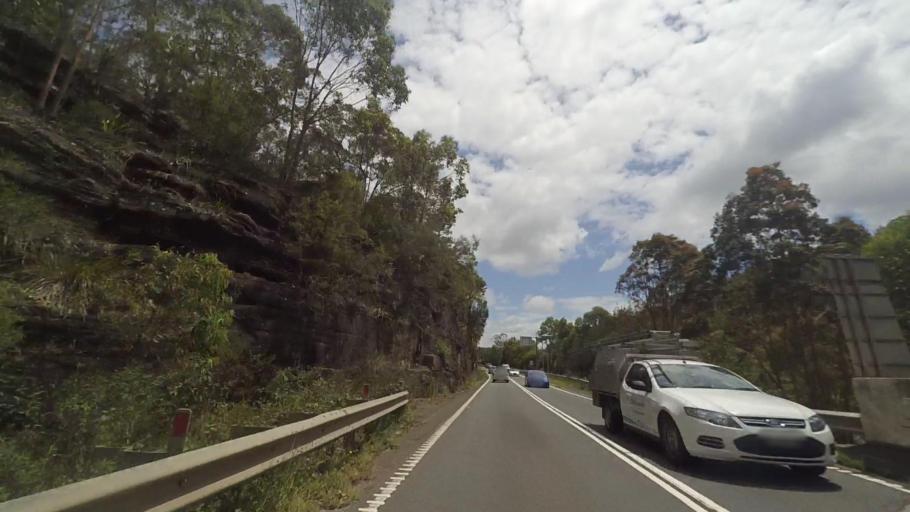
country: AU
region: New South Wales
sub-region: Sutherland Shire
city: Engadine
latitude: -34.0615
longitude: 150.9962
